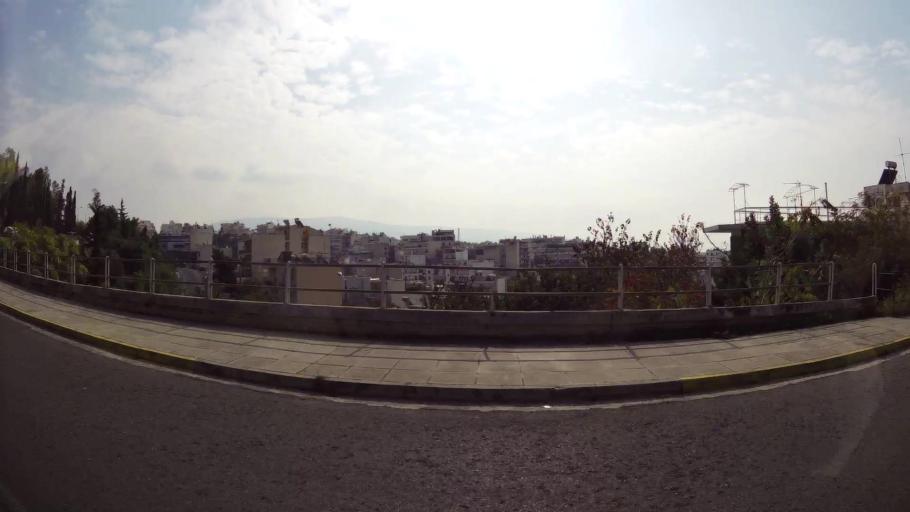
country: GR
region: Attica
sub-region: Nomarchia Athinas
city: Galatsi
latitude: 38.0001
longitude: 23.7551
